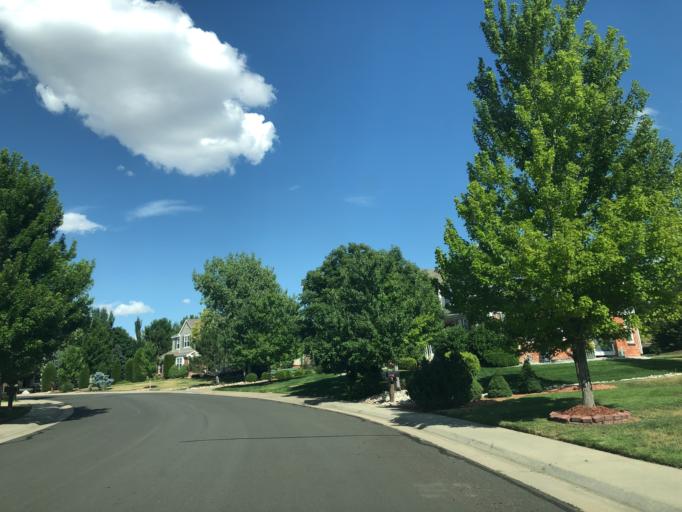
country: US
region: Colorado
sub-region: Arapahoe County
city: Dove Valley
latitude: 39.5958
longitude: -104.7762
